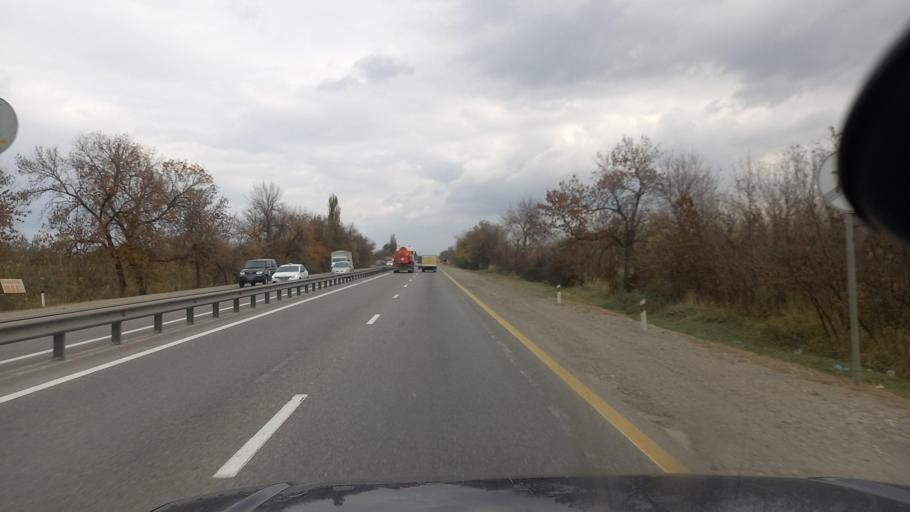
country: RU
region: Krasnodarskiy
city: Afipskiy
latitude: 44.8966
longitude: 38.8645
